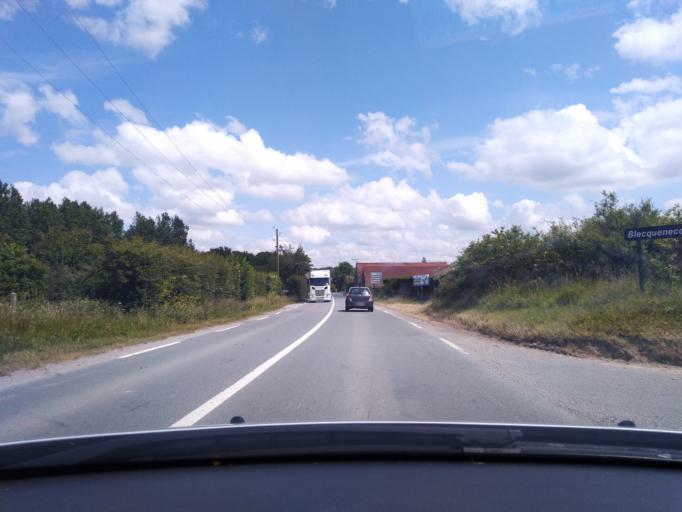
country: FR
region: Nord-Pas-de-Calais
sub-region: Departement du Pas-de-Calais
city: Rinxent
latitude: 50.8224
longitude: 1.7245
